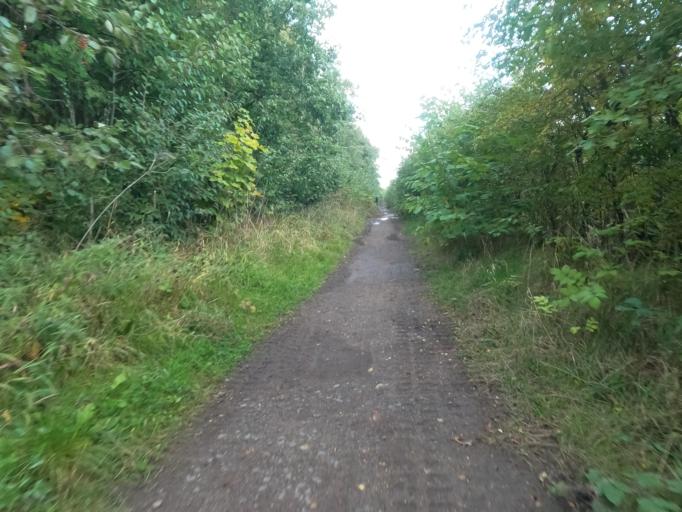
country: GB
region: England
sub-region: Northumberland
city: Seghill
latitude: 55.0702
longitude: -1.5471
